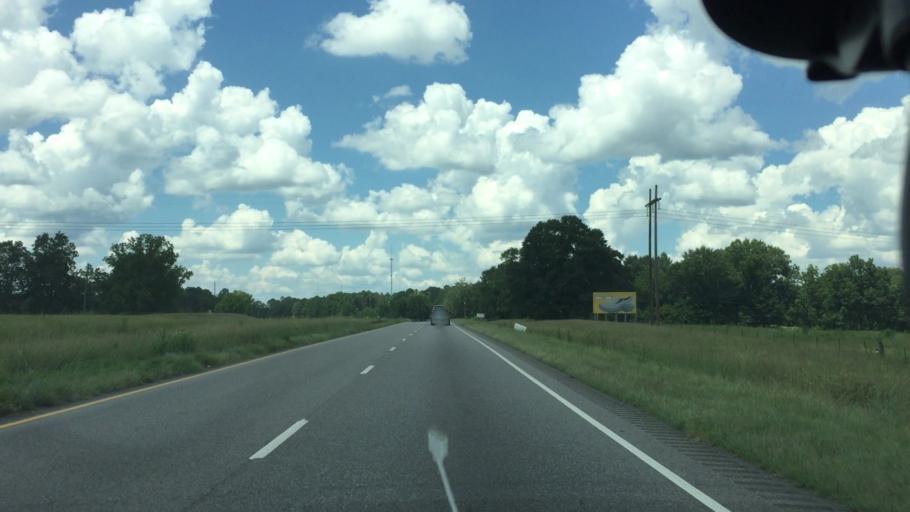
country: US
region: Alabama
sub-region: Montgomery County
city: Taylor
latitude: 32.0351
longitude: -86.0327
